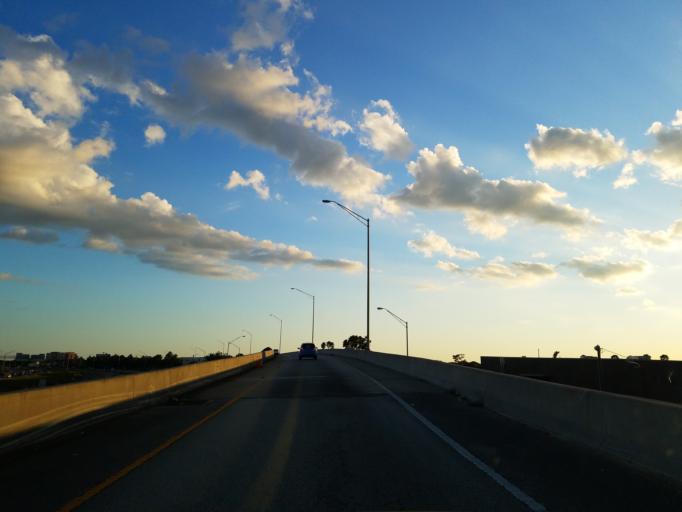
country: US
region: Florida
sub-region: Orange County
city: Doctor Phillips
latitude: 28.4608
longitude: -81.4718
